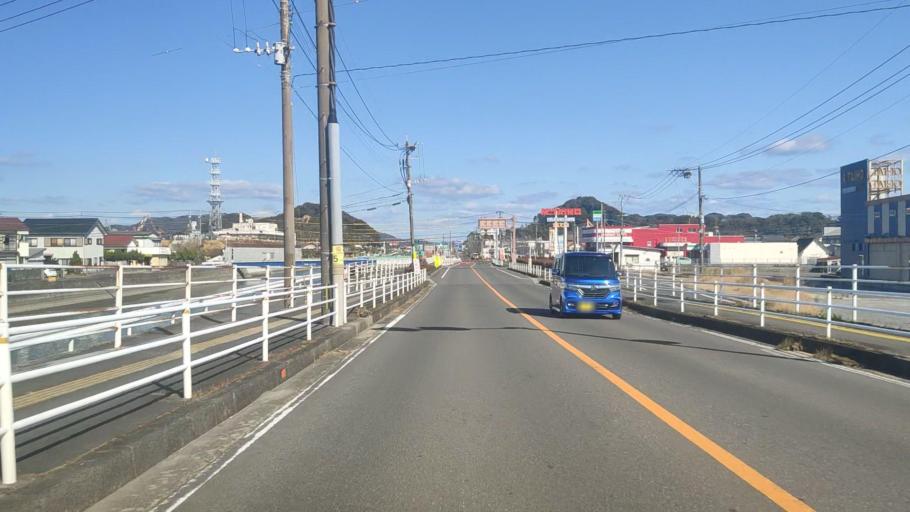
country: JP
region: Oita
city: Saiki
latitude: 32.9506
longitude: 131.9047
